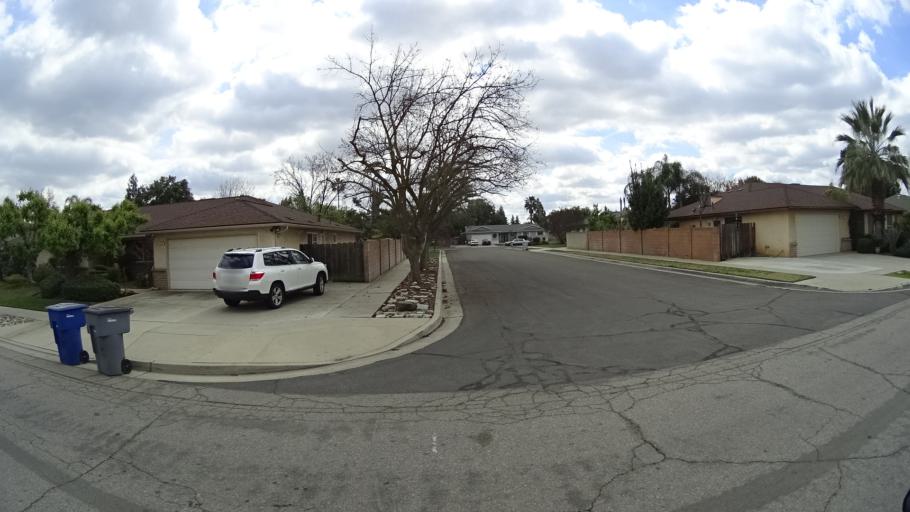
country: US
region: California
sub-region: Fresno County
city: Fresno
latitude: 36.8340
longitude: -119.8194
